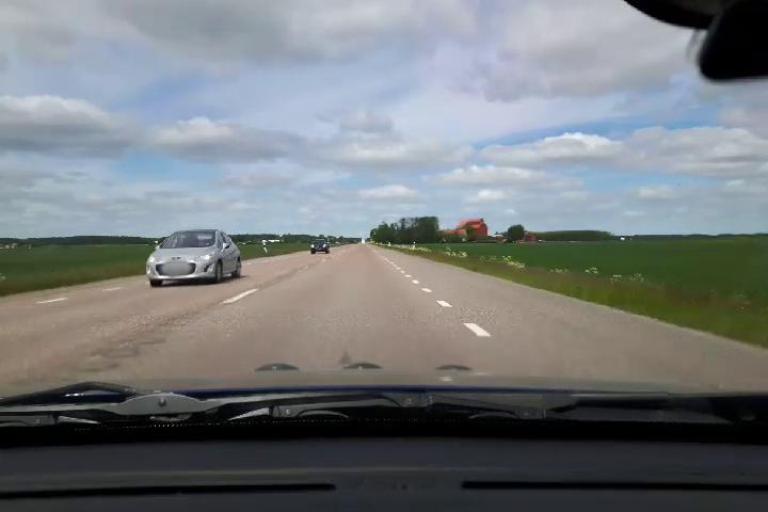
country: SE
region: Uppsala
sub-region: Uppsala Kommun
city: Gamla Uppsala
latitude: 59.9157
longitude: 17.6050
